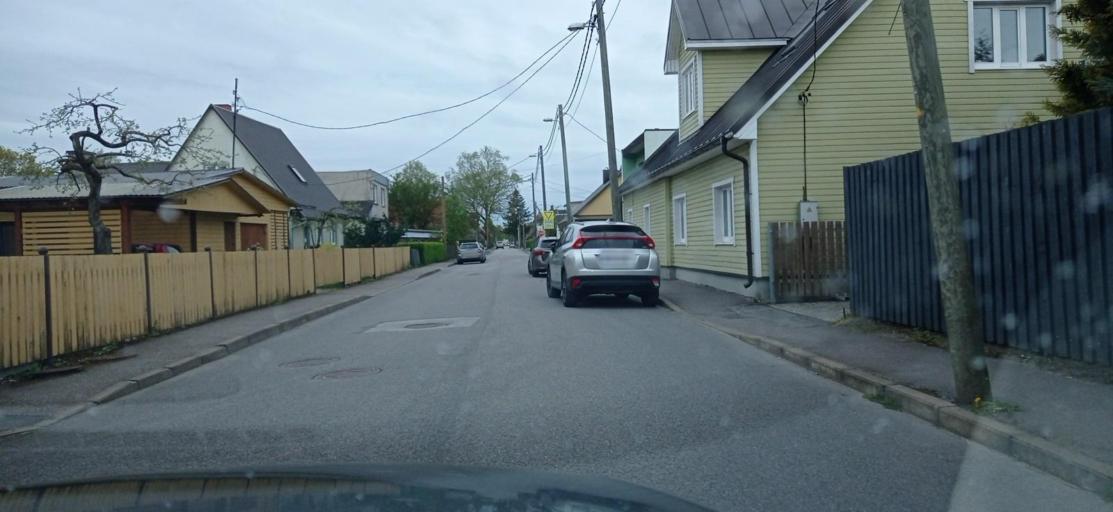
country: EE
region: Paernumaa
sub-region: Paernu linn
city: Parnu
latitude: 58.3973
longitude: 24.4899
